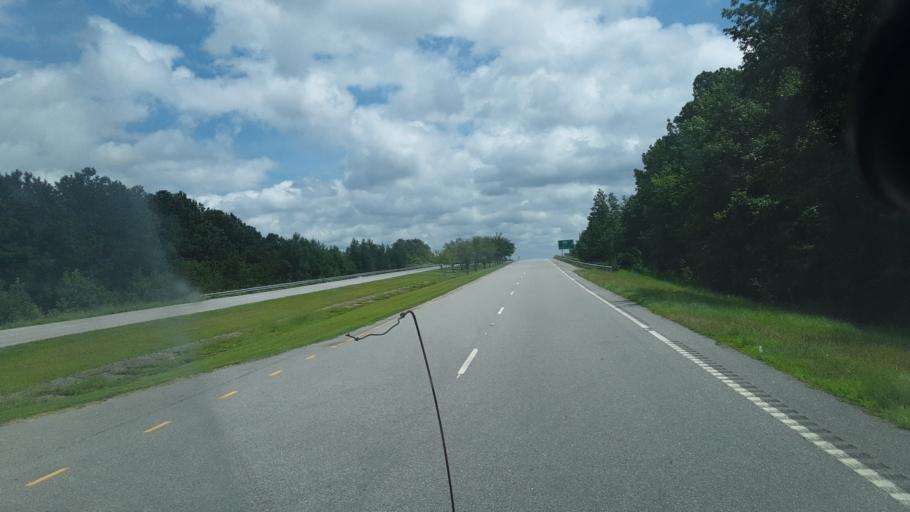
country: US
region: South Carolina
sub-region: Horry County
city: Loris
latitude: 34.0837
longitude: -78.8785
